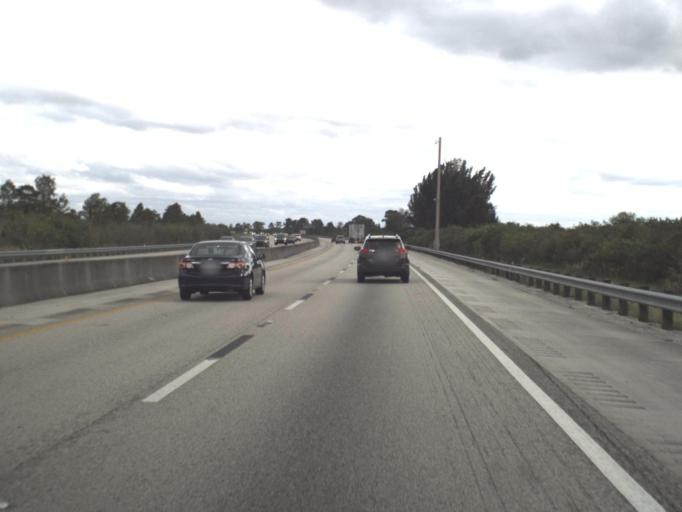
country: US
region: Florida
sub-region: Martin County
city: Hobe Sound
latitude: 27.0310
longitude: -80.2363
